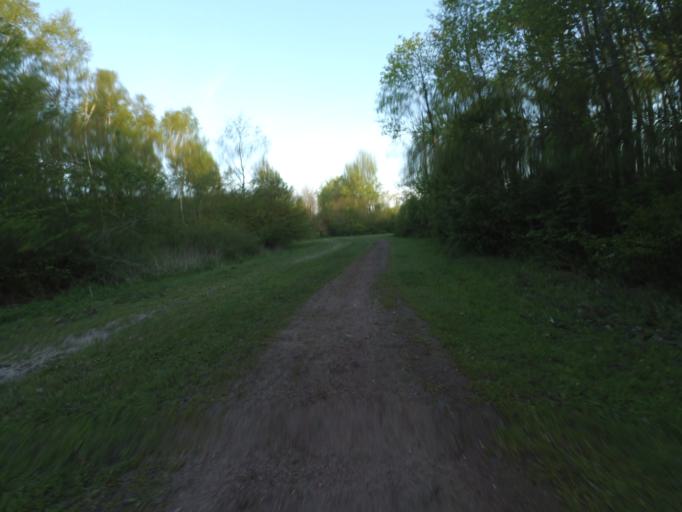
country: NL
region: Flevoland
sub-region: Gemeente Zeewolde
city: Zeewolde
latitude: 52.4156
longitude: 5.4999
